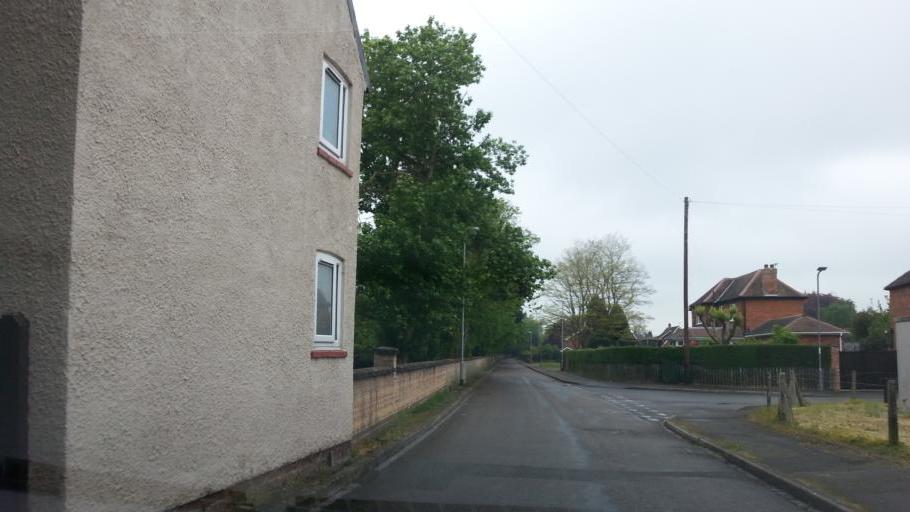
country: GB
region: England
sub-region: Nottinghamshire
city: Newark on Trent
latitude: 53.0655
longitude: -0.7983
